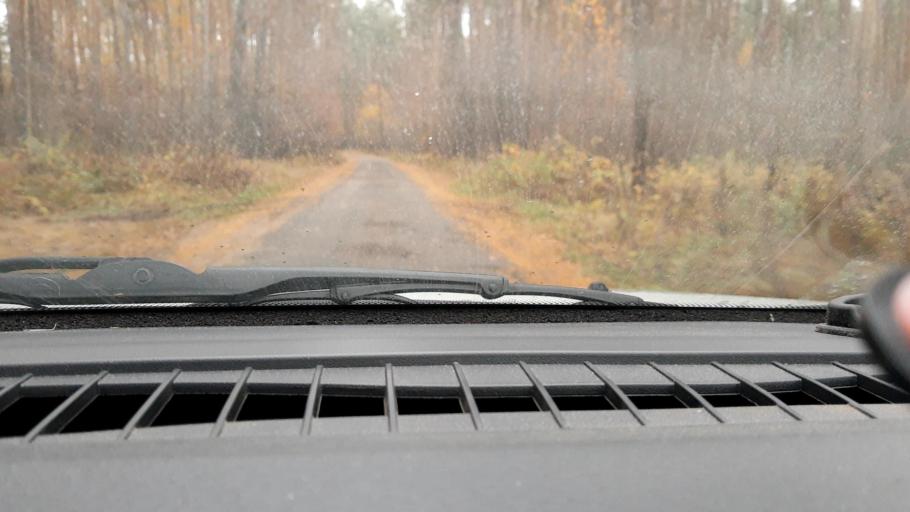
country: RU
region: Nizjnij Novgorod
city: Sitniki
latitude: 56.4178
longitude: 44.0436
